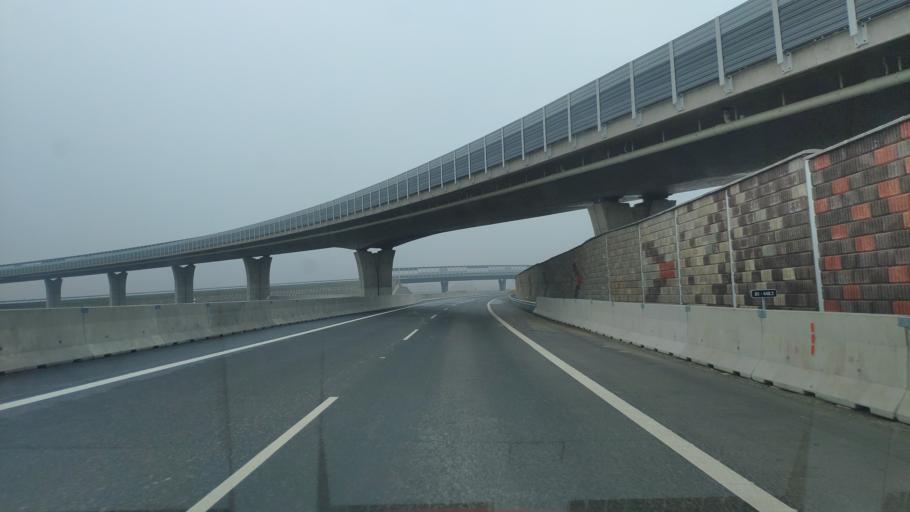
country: SK
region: Kosicky
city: Kosice
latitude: 48.7423
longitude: 21.3404
